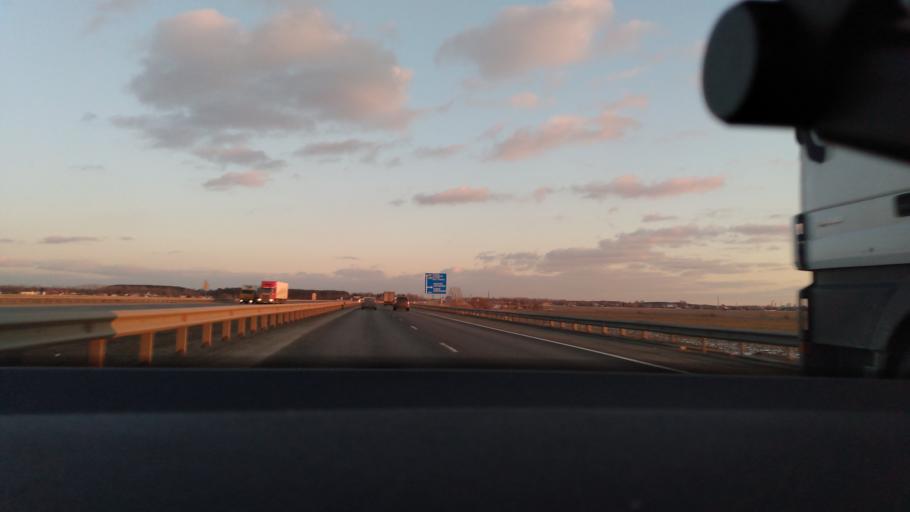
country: RU
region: Moskovskaya
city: Raduzhnyy
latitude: 55.1386
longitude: 38.7621
